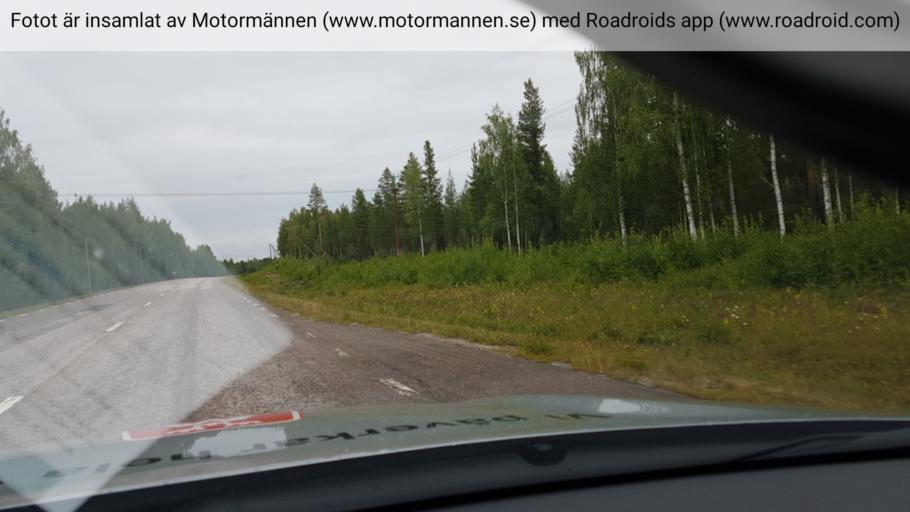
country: SE
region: Norrbotten
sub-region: Alvsbyns Kommun
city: AElvsbyn
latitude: 66.1845
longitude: 20.8789
